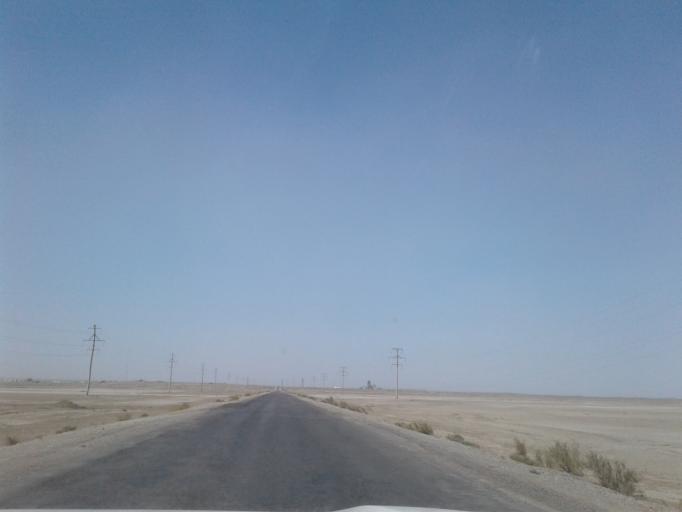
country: TM
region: Balkan
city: Gumdag
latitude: 39.0951
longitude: 54.5846
